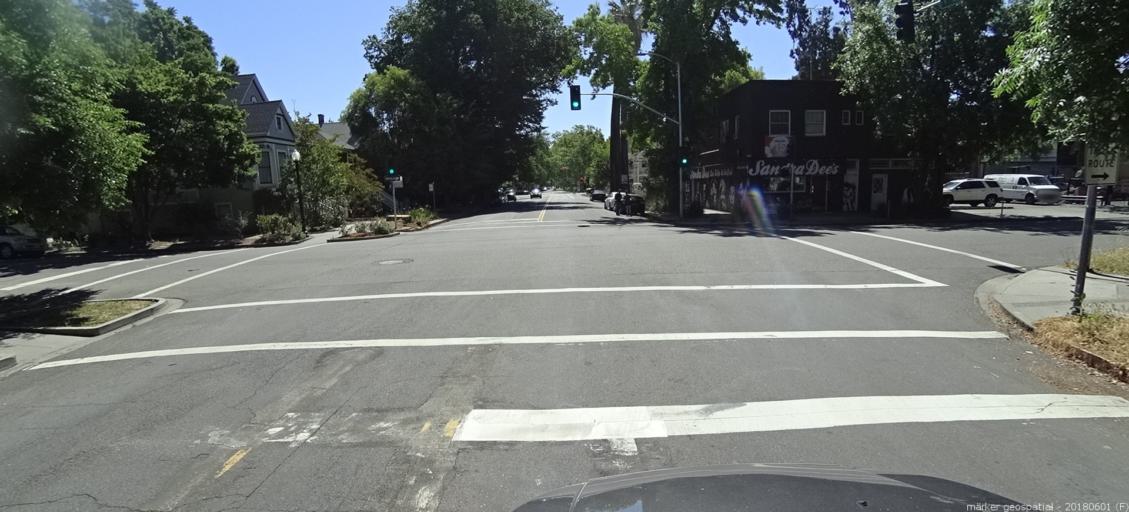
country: US
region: California
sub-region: Sacramento County
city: Sacramento
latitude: 38.5829
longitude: -121.4849
